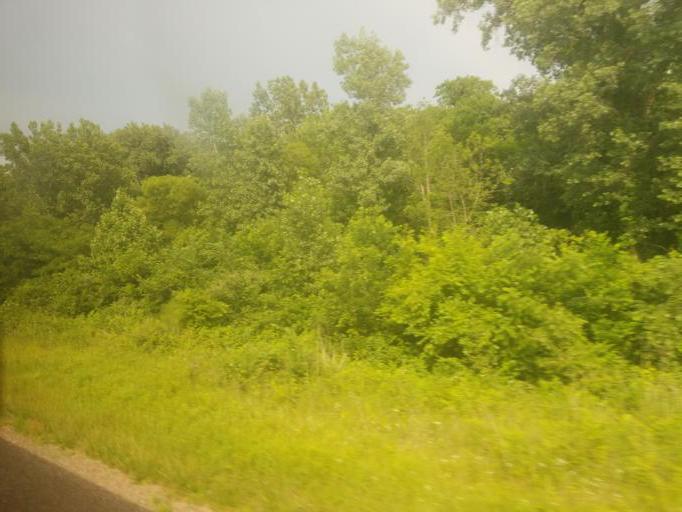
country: US
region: Illinois
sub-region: Bureau County
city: Princeton
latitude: 41.3298
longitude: -89.6757
